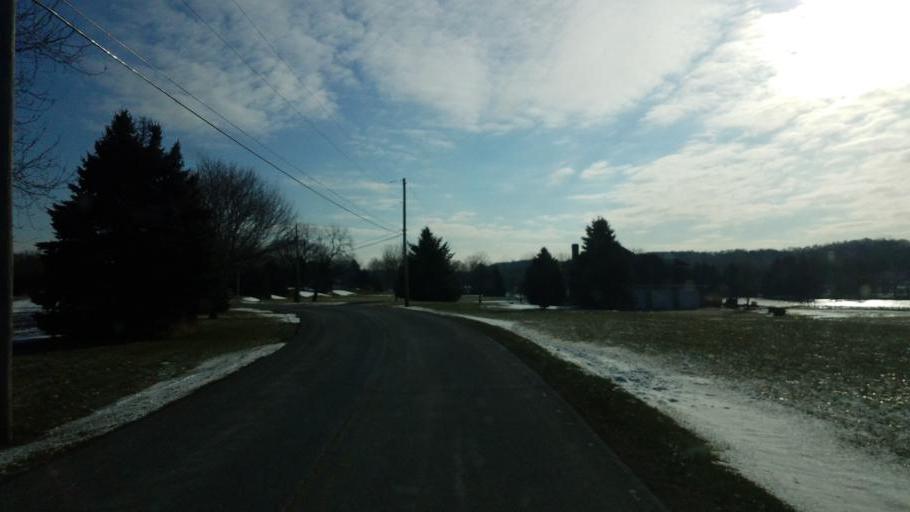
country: US
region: Ohio
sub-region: Sandusky County
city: Bellville
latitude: 40.6190
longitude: -82.5661
